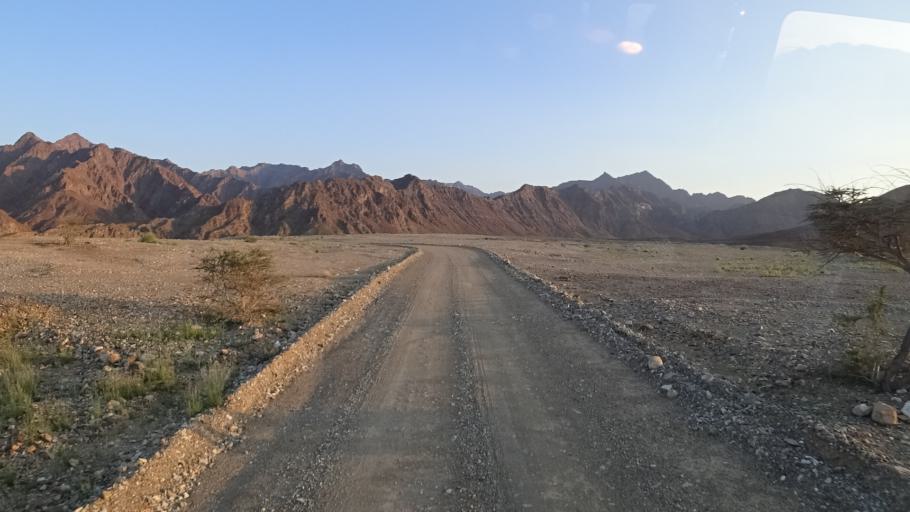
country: OM
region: Al Batinah
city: Al Khaburah
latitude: 23.7511
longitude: 56.9242
